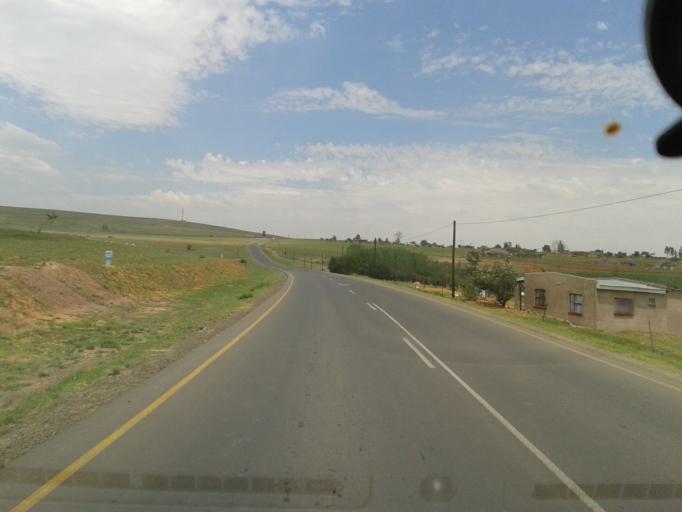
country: LS
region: Maseru
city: Maseru
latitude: -29.3650
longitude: 27.6463
